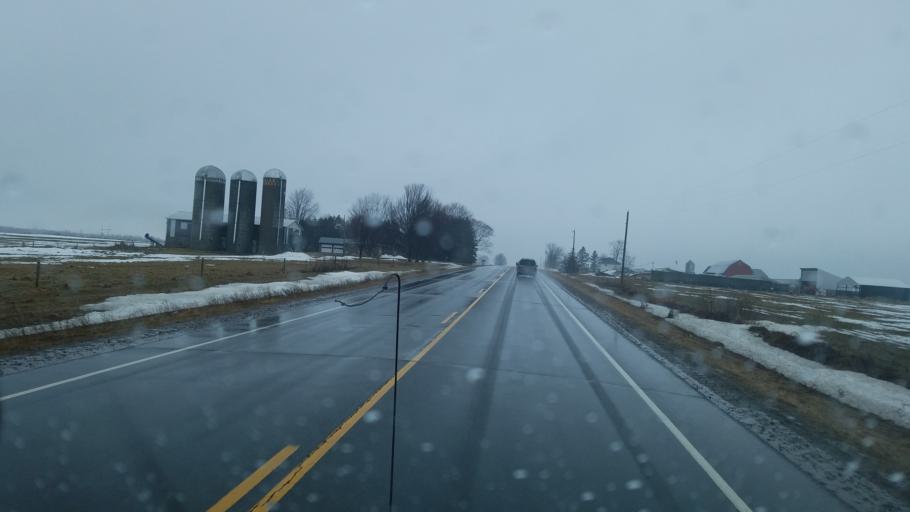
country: US
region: Wisconsin
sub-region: Marathon County
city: Spencer
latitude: 44.6562
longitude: -90.3285
